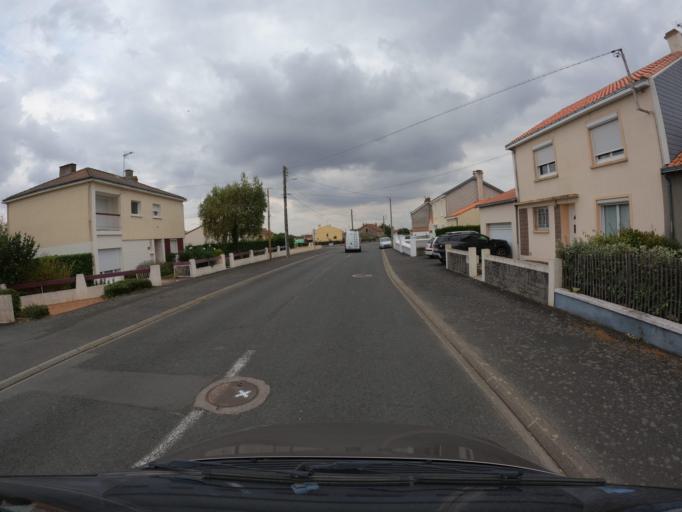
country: FR
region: Pays de la Loire
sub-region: Departement de Maine-et-Loire
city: Le Longeron
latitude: 47.0214
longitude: -1.0559
